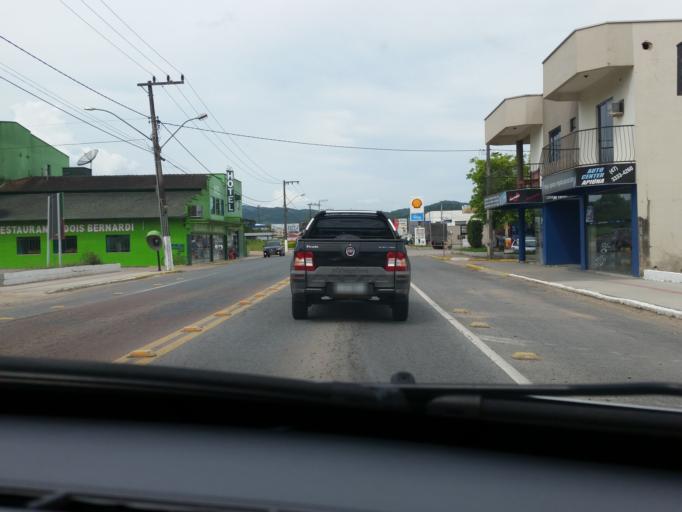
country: BR
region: Santa Catarina
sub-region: Ibirama
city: Ibirama
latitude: -27.0378
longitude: -49.3932
